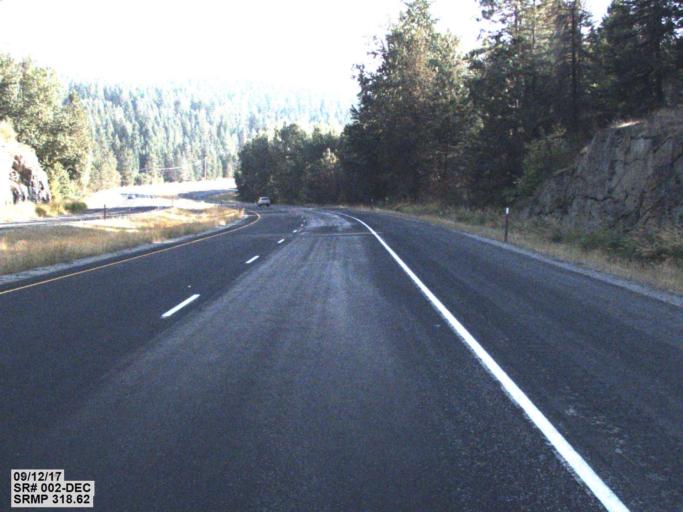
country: US
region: Washington
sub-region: Spokane County
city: Deer Park
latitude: 48.0868
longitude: -117.3258
